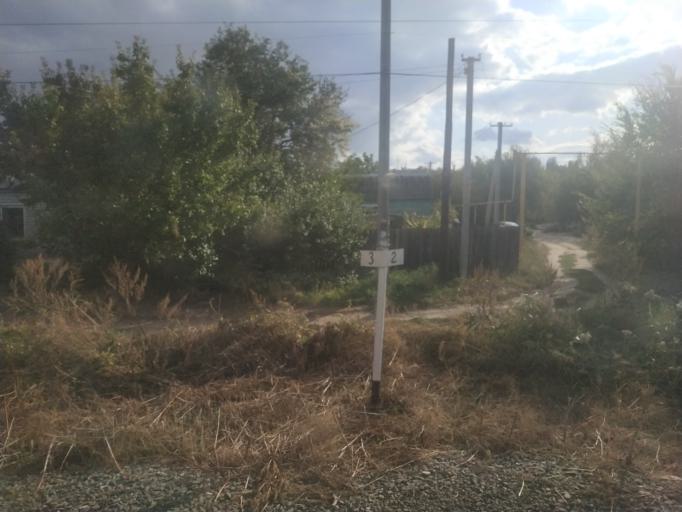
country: RU
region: Volgograd
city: Krasnoslobodsk
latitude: 48.5094
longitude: 44.5341
